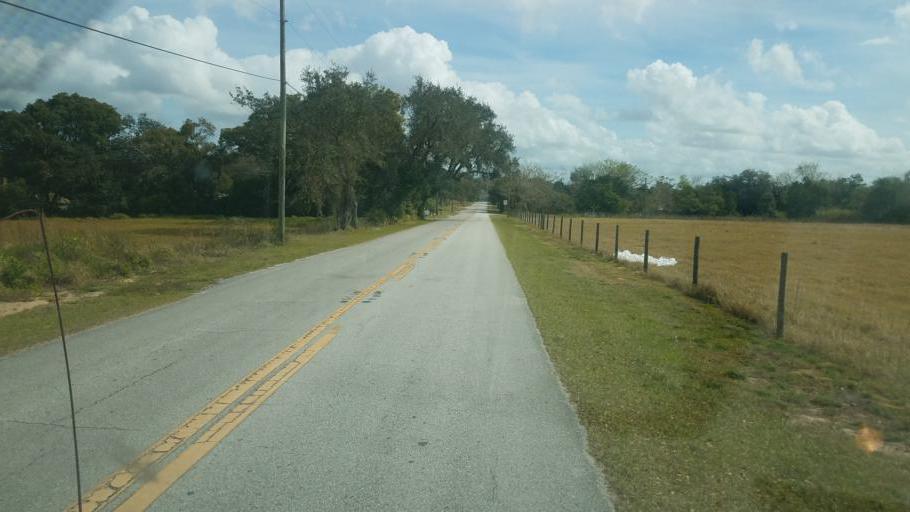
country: US
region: Florida
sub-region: Polk County
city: Dundee
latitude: 28.0334
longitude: -81.6111
